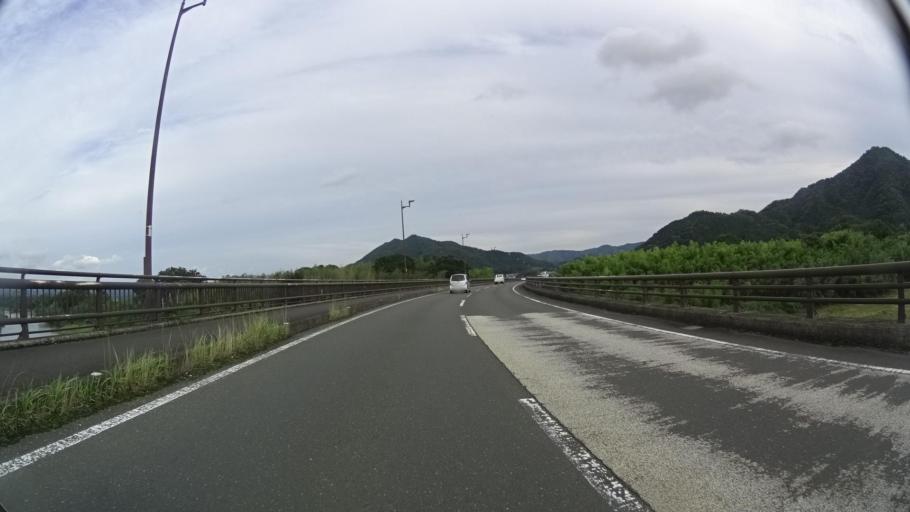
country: JP
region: Kyoto
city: Ayabe
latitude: 35.3087
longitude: 135.2296
